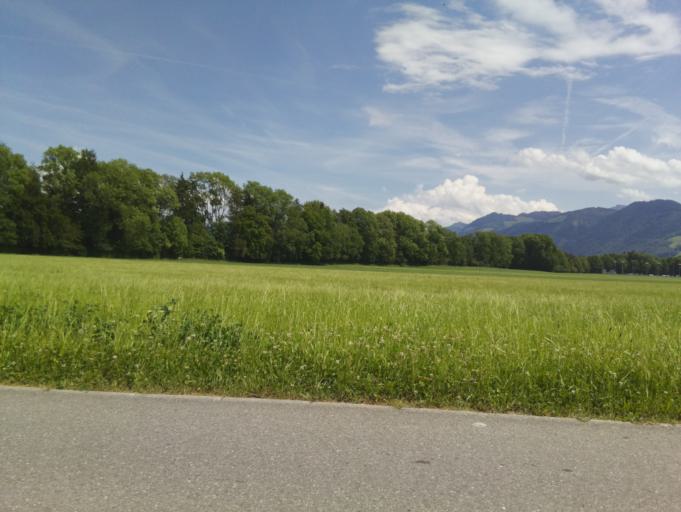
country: CH
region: Schwyz
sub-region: Bezirk March
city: Lachen
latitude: 47.1996
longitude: 8.8608
